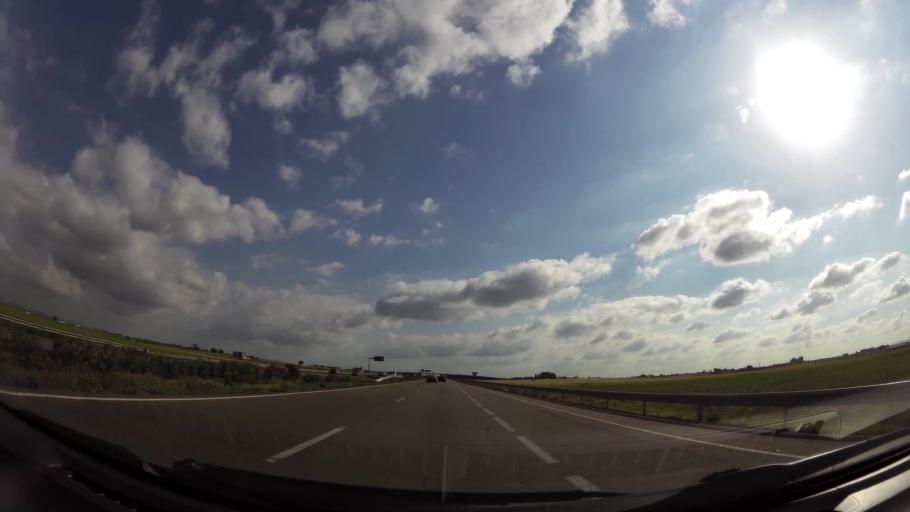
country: MA
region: Chaouia-Ouardigha
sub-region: Settat Province
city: Berrechid
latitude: 33.2446
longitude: -7.5661
